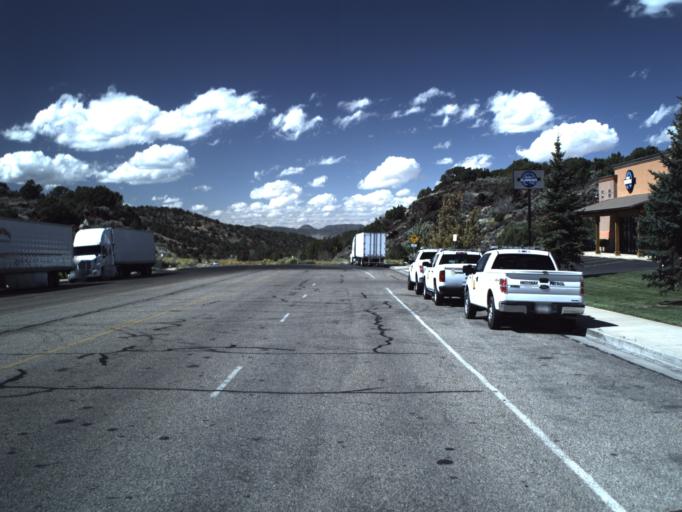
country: US
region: Utah
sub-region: Iron County
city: Cedar City
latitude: 37.6556
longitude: -113.0871
